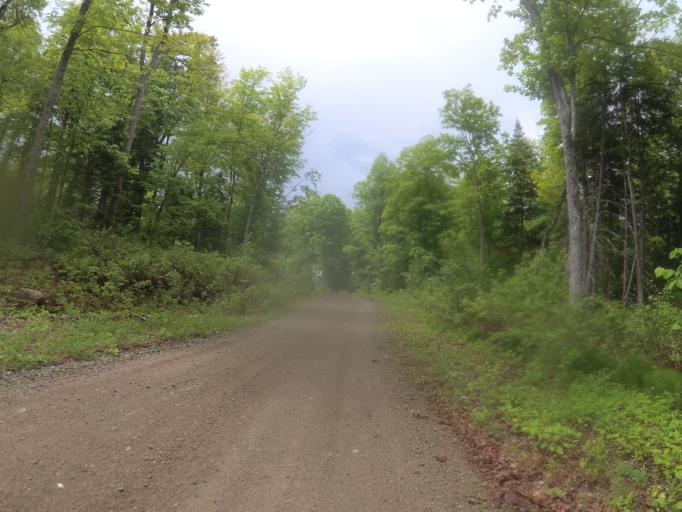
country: CA
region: Ontario
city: Renfrew
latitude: 45.1270
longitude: -76.8165
